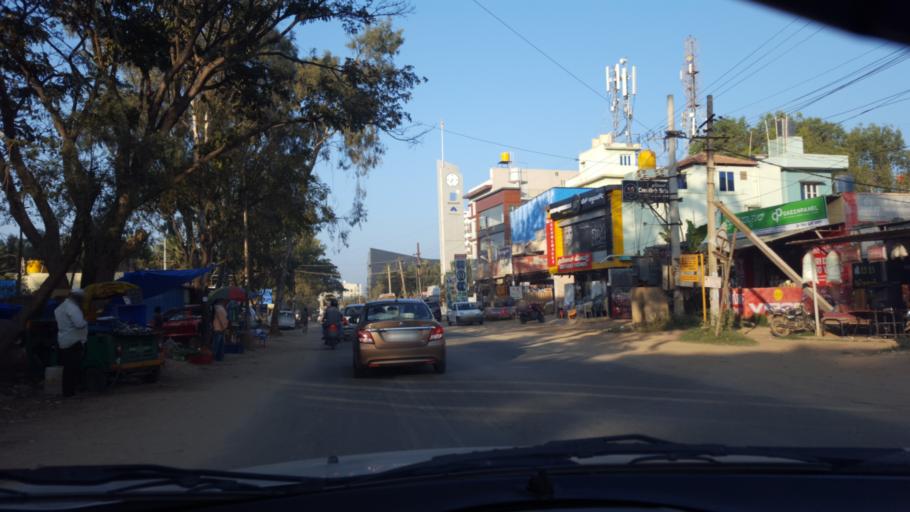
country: IN
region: Karnataka
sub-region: Bangalore Rural
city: Hoskote
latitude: 12.9331
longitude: 77.7427
